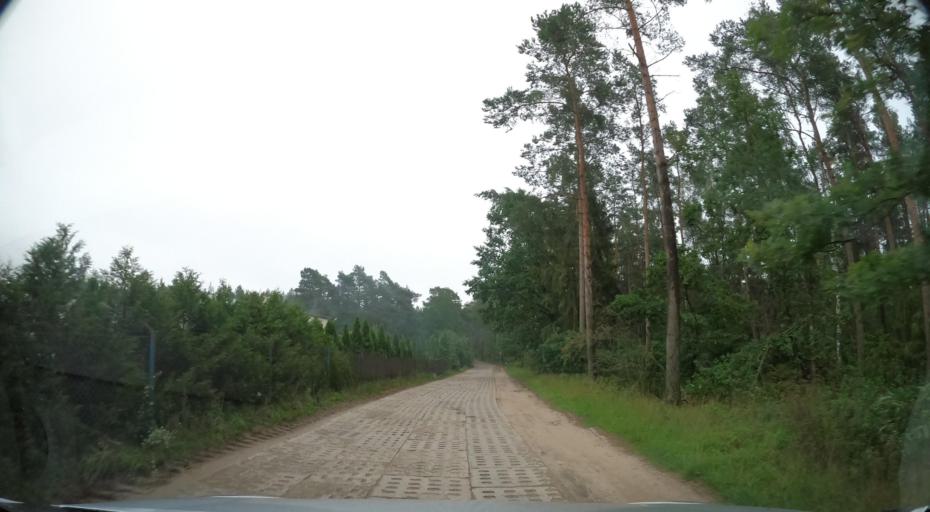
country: PL
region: Pomeranian Voivodeship
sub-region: Powiat kartuski
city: Chwaszczyno
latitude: 54.4207
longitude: 18.4210
